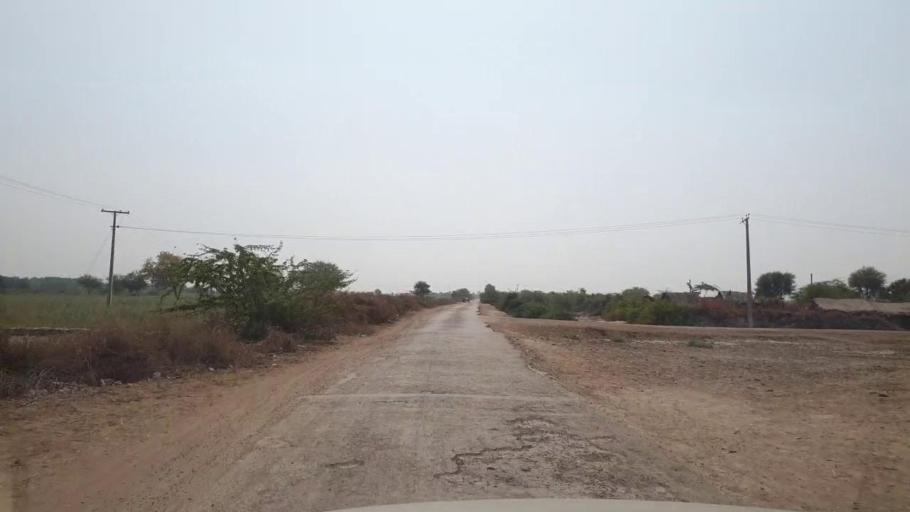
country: PK
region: Sindh
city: Dhoro Naro
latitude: 25.4746
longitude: 69.6386
